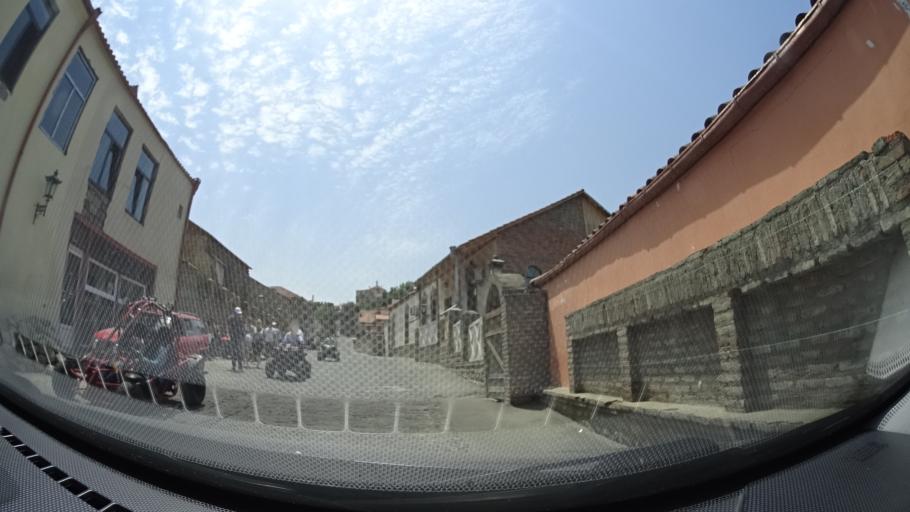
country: GE
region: Kakheti
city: Sighnaghi
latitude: 41.6225
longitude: 45.9236
